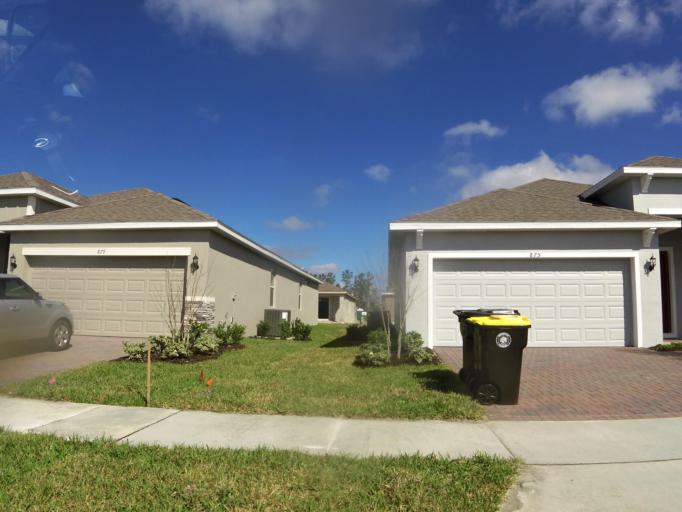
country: US
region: Florida
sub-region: Volusia County
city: Orange City
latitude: 28.9360
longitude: -81.3114
